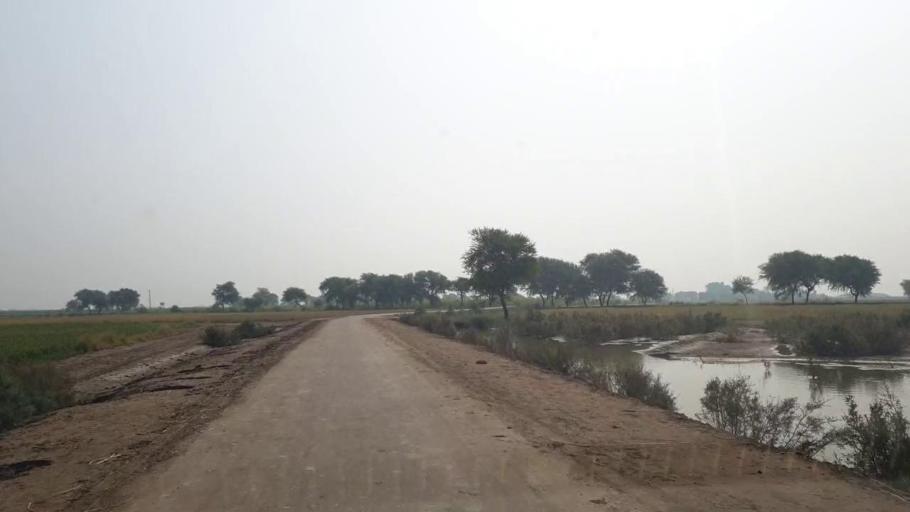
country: PK
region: Sindh
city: Matli
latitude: 25.1300
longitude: 68.7032
